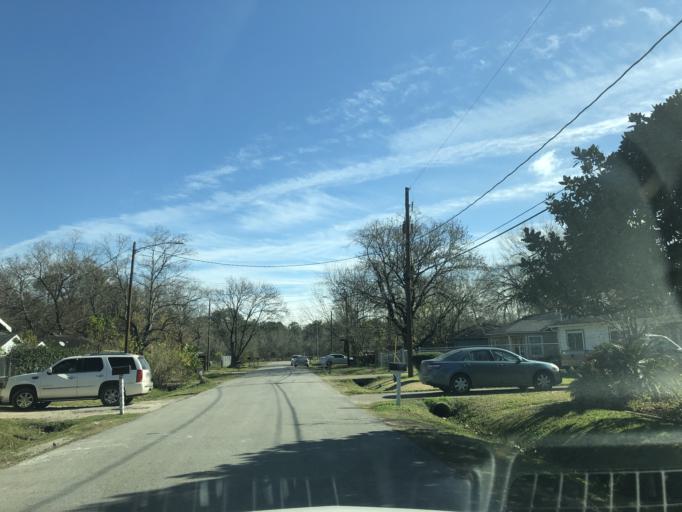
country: US
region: Texas
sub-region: Harris County
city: Jacinto City
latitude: 29.8386
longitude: -95.2903
